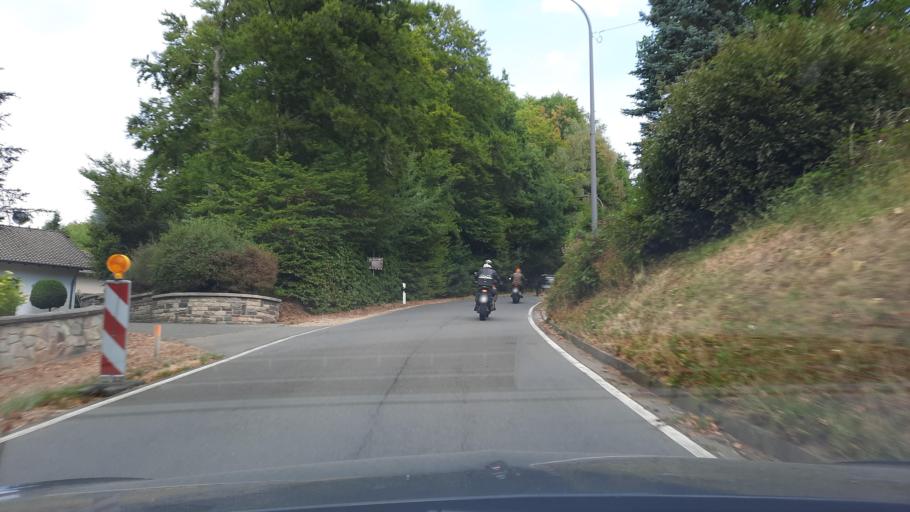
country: DE
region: Rheinland-Pfalz
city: Watzerath
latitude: 50.1950
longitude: 6.3673
